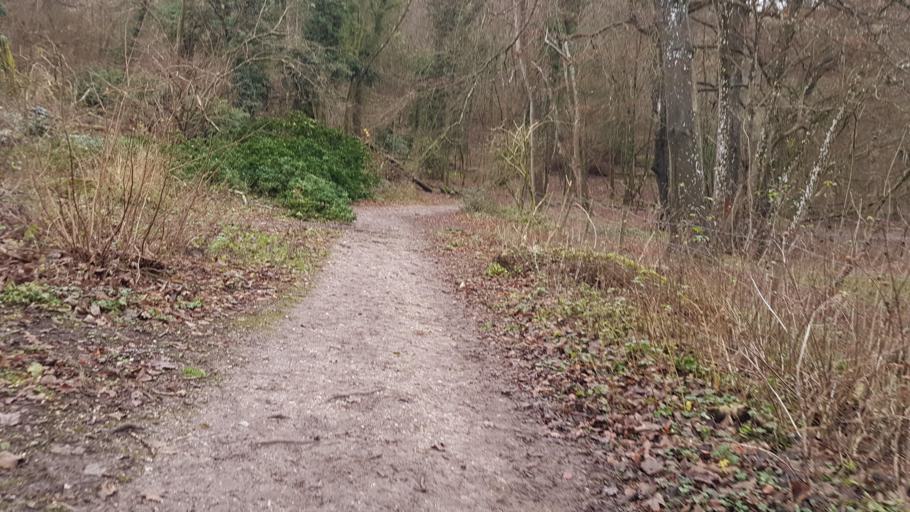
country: GB
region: England
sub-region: West Sussex
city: Steyning
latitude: 50.8824
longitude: -0.3470
